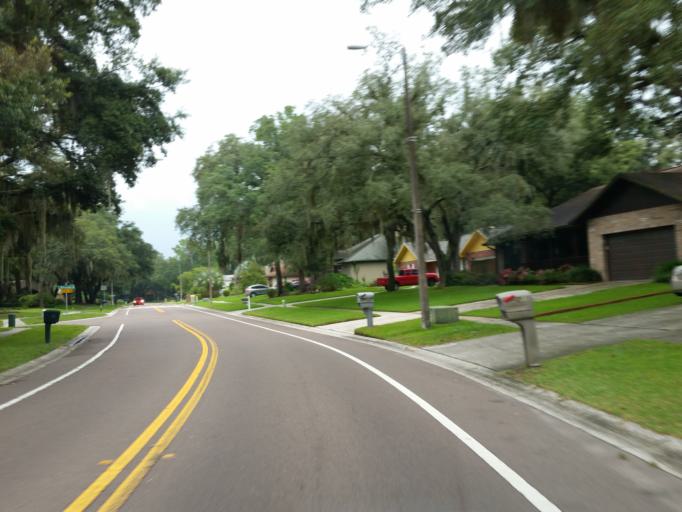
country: US
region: Florida
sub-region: Hillsborough County
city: Bloomingdale
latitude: 27.8841
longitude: -82.2819
